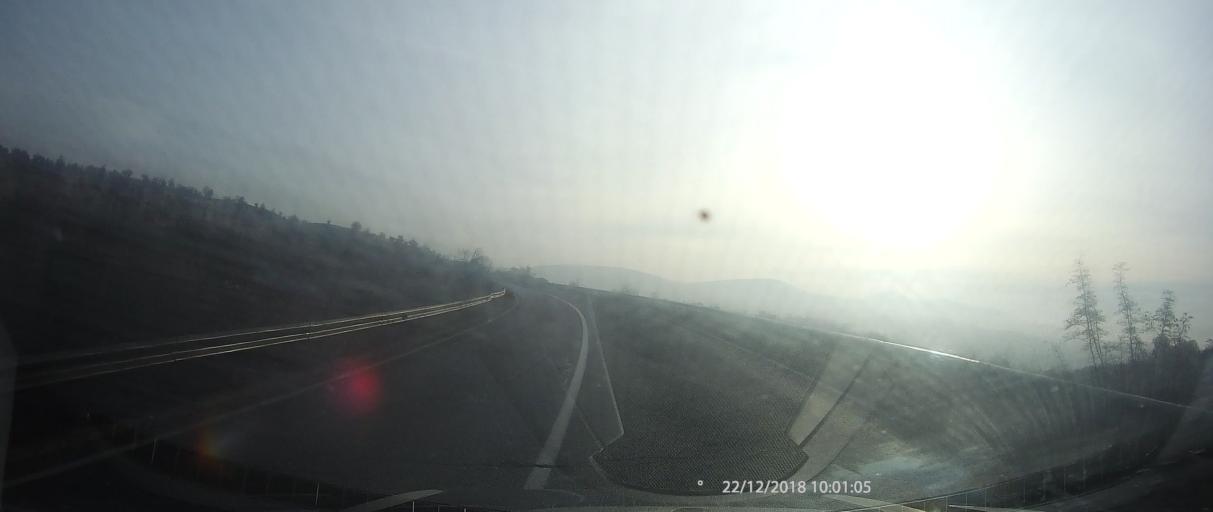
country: MK
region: Opstina Rankovce
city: Rankovce
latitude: 42.1454
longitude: 21.9896
